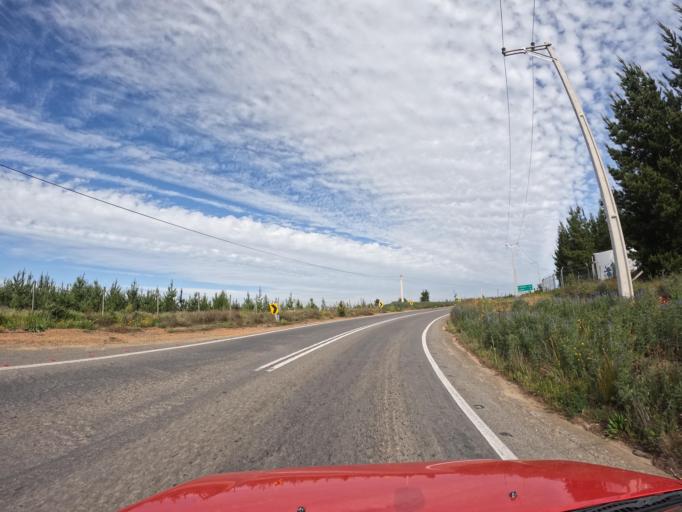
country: CL
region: O'Higgins
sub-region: Provincia de Colchagua
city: Santa Cruz
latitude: -34.3078
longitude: -71.8498
